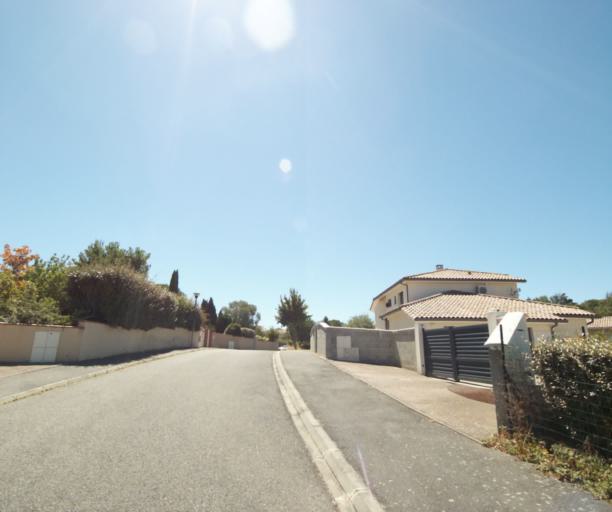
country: FR
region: Midi-Pyrenees
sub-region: Departement de la Haute-Garonne
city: Pechabou
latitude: 43.5057
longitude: 1.5009
